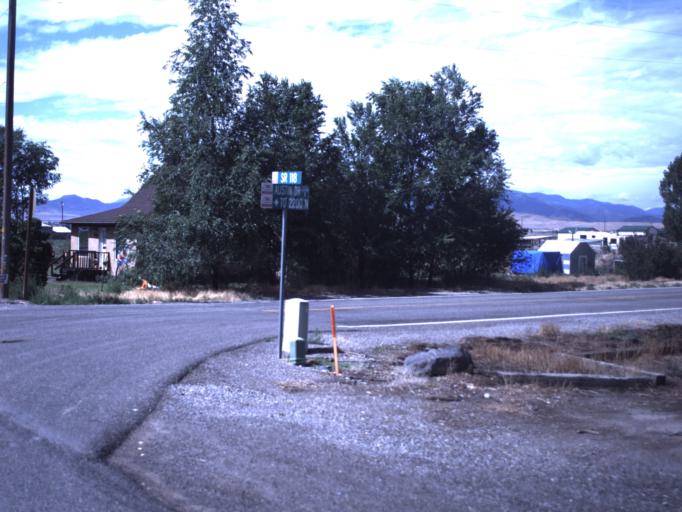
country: US
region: Utah
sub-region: Sevier County
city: Monroe
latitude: 38.6697
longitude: -112.1209
